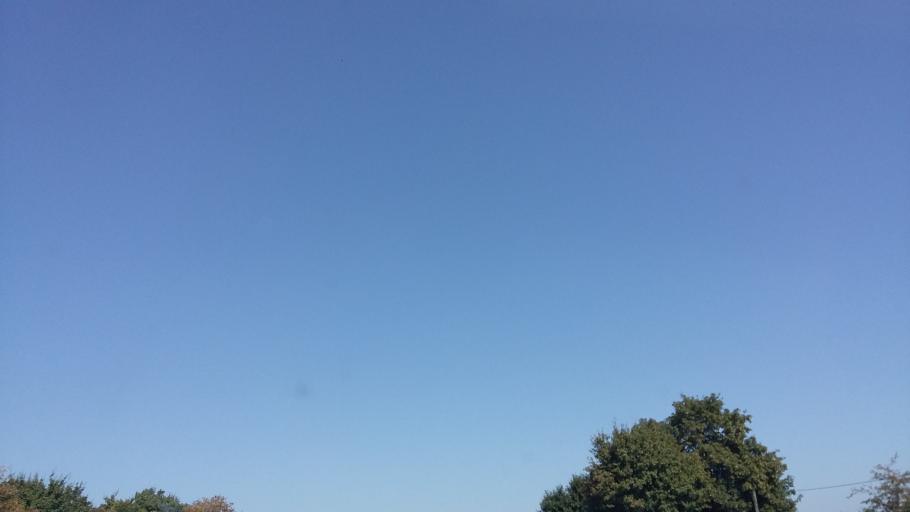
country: DE
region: Bavaria
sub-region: Swabia
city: Oberottmarshausen
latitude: 48.2101
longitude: 10.8589
